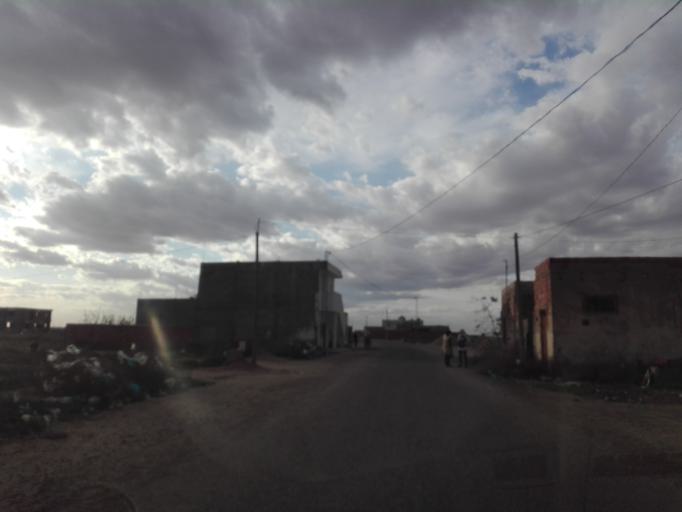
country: TN
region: Safaqis
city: Al Qarmadah
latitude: 34.8057
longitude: 10.8601
